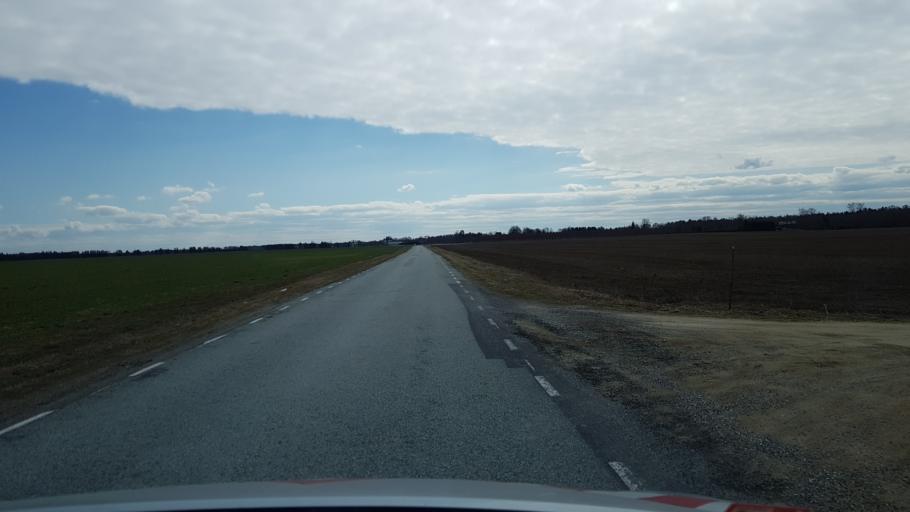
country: EE
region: Laeaene-Virumaa
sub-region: Haljala vald
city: Haljala
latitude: 59.4122
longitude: 26.2531
